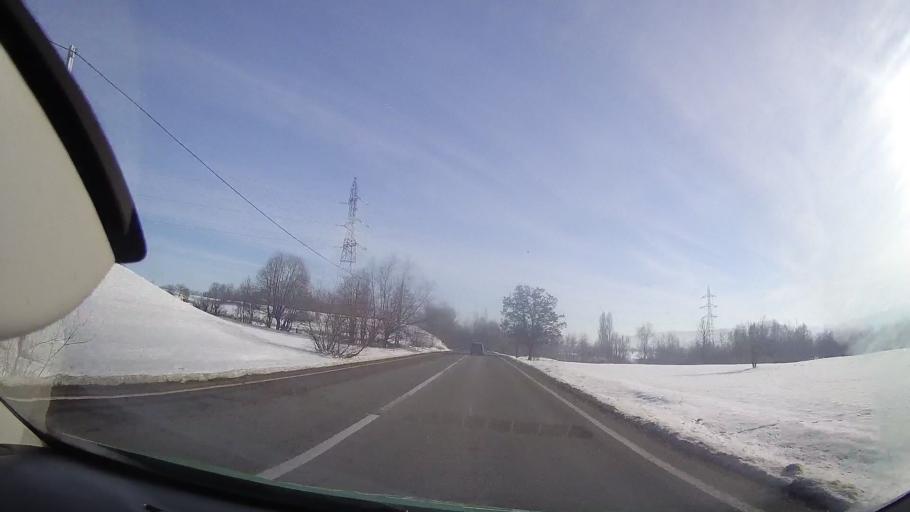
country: RO
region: Neamt
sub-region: Comuna Ghindaoani
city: Ghindaoani
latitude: 47.0741
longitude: 26.3574
